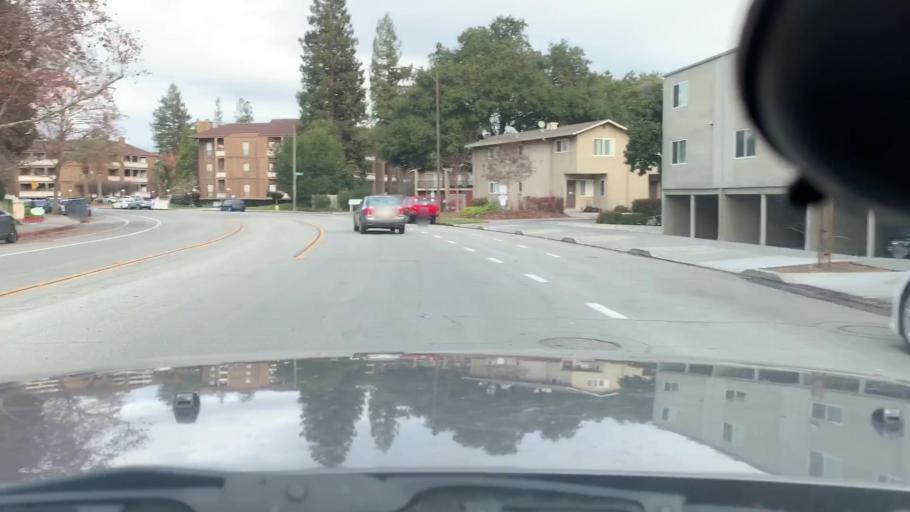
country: US
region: California
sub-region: Santa Clara County
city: Campbell
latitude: 37.3018
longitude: -121.9767
